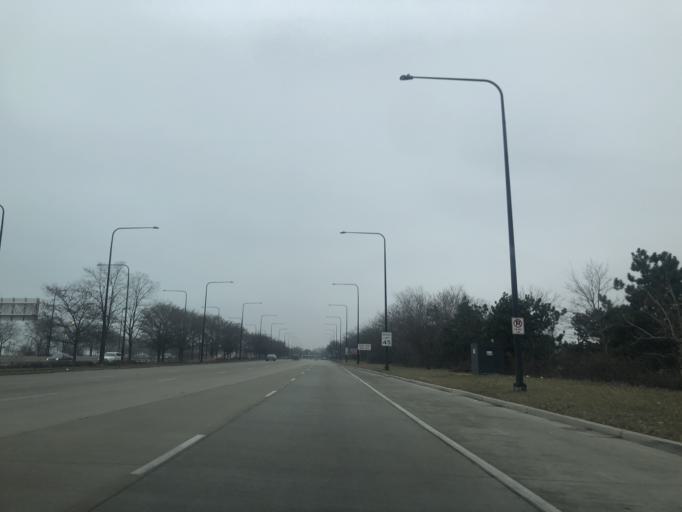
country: US
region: Illinois
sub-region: Cook County
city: Chicago
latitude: 41.8445
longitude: -87.6113
